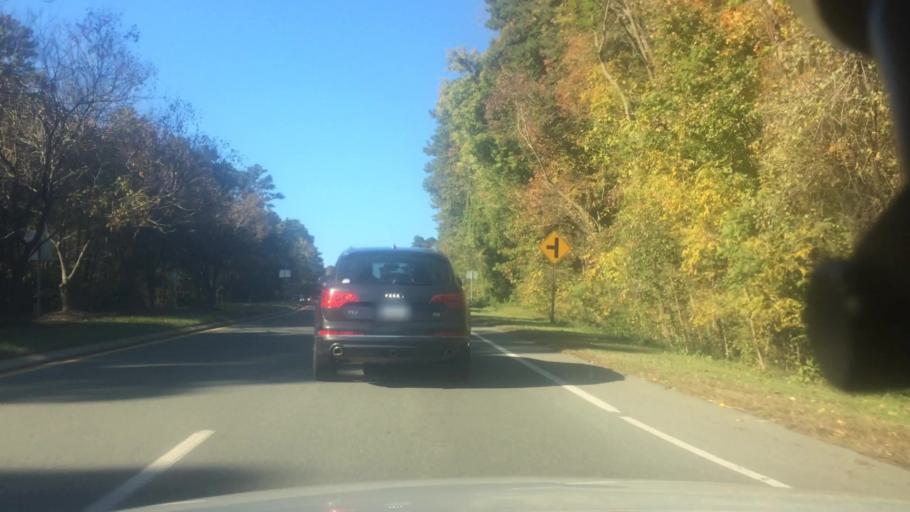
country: US
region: North Carolina
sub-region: Orange County
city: Chapel Hill
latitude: 35.8971
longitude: -79.0407
